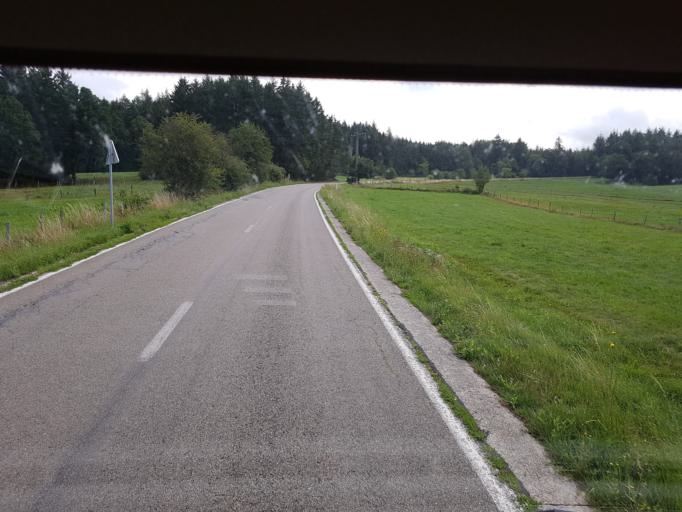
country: BE
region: Wallonia
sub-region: Province de Liege
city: Saint-Vith
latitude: 50.2597
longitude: 6.1512
